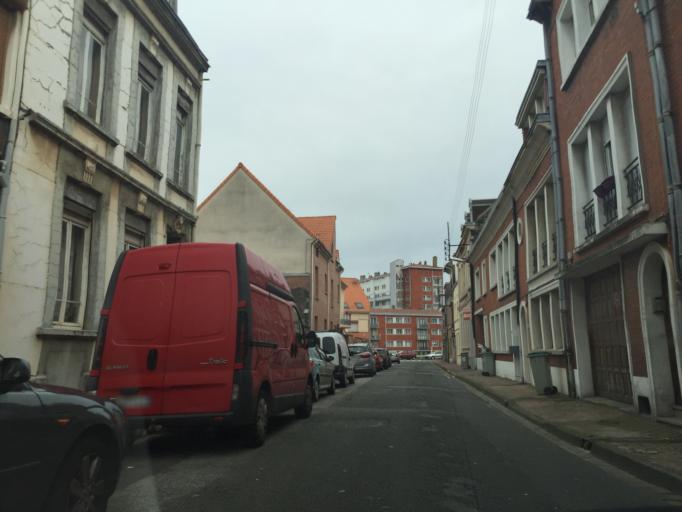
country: FR
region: Nord-Pas-de-Calais
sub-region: Departement du Pas-de-Calais
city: Calais
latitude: 50.9479
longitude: 1.8613
